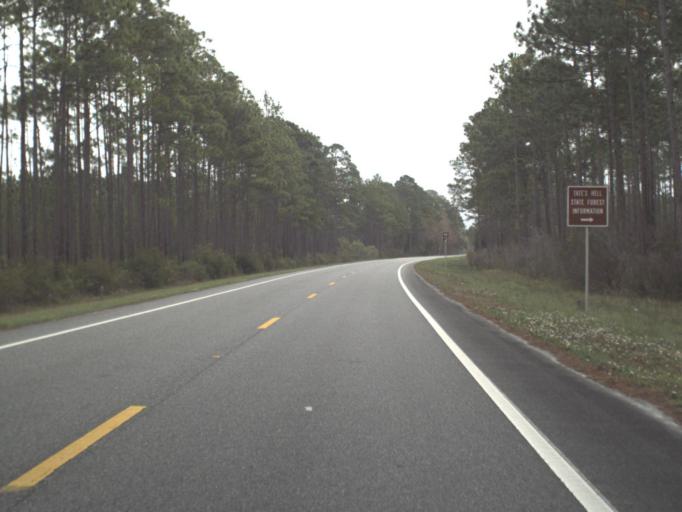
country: US
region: Florida
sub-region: Franklin County
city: Eastpoint
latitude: 29.8290
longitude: -84.8924
